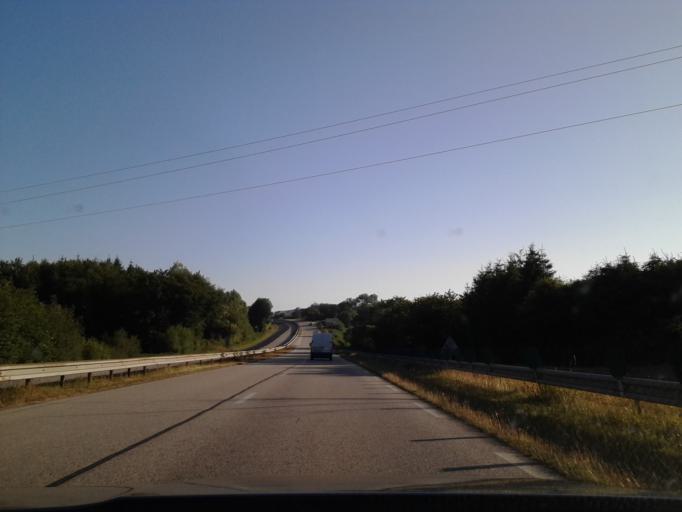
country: FR
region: Lower Normandy
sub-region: Departement de la Manche
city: La Glacerie
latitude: 49.5900
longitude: -1.5964
